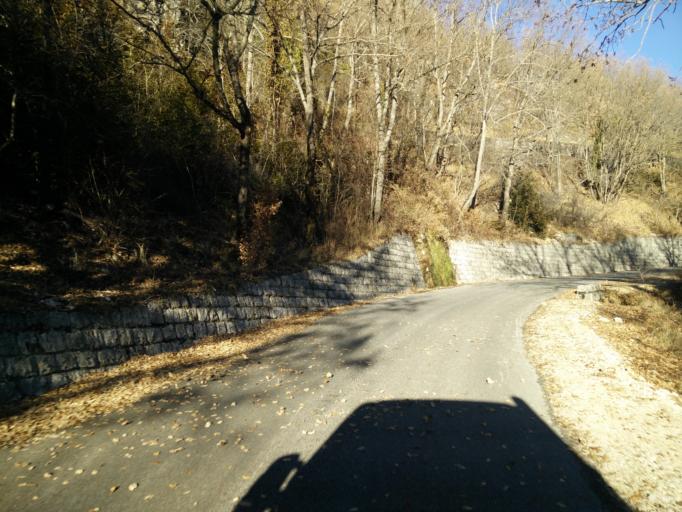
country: FR
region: Provence-Alpes-Cote d'Azur
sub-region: Departement des Alpes-de-Haute-Provence
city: Castellane
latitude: 43.7935
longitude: 6.4044
